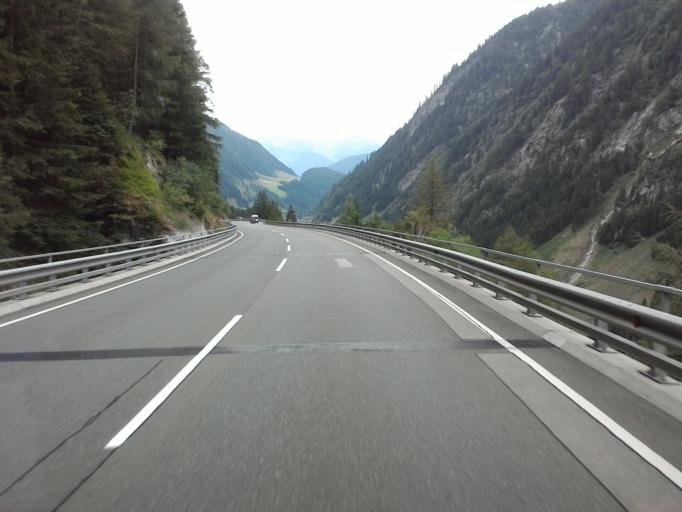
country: AT
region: Tyrol
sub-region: Politischer Bezirk Lienz
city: Matrei in Osttirol
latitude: 47.0866
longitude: 12.5304
